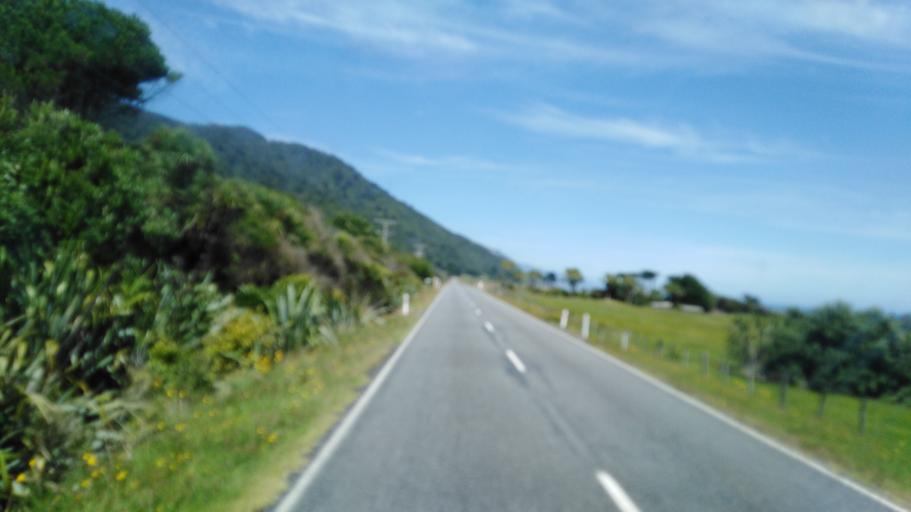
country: NZ
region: West Coast
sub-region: Buller District
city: Westport
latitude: -41.5536
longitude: 171.9205
